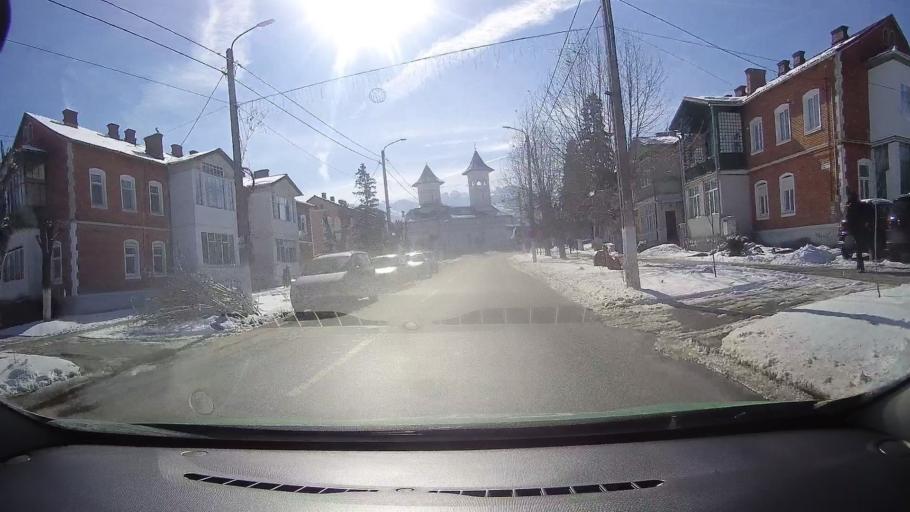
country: RO
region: Brasov
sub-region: Oras Victoria
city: Victoria
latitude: 45.7265
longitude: 24.7018
